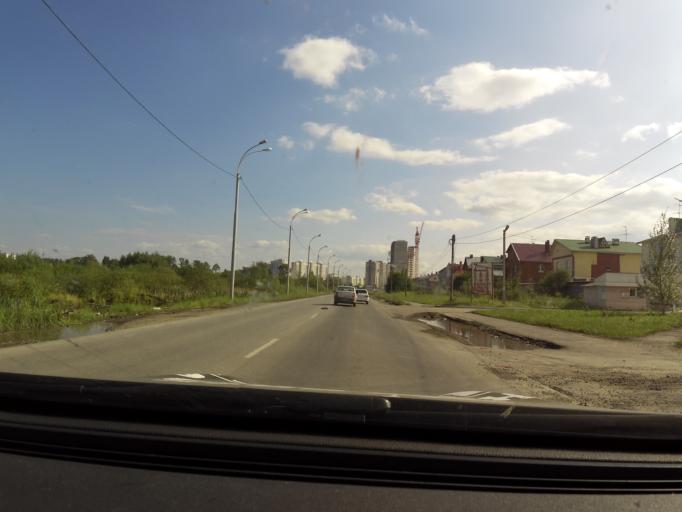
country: RU
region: Sverdlovsk
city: Shirokaya Rechka
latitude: 56.8044
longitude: 60.4946
